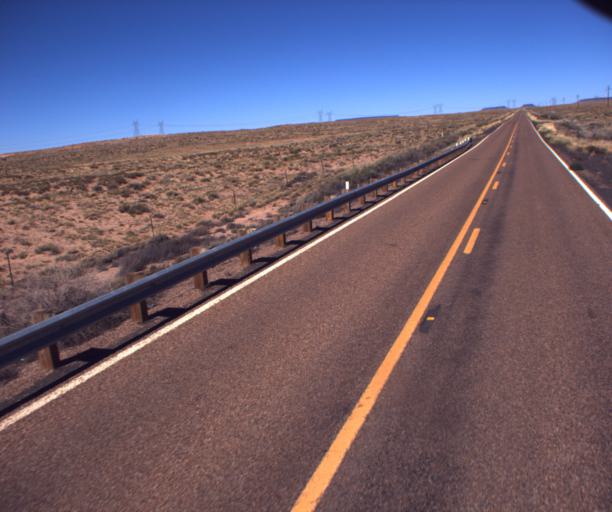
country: US
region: Arizona
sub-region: Navajo County
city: Holbrook
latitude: 35.1439
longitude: -110.0888
